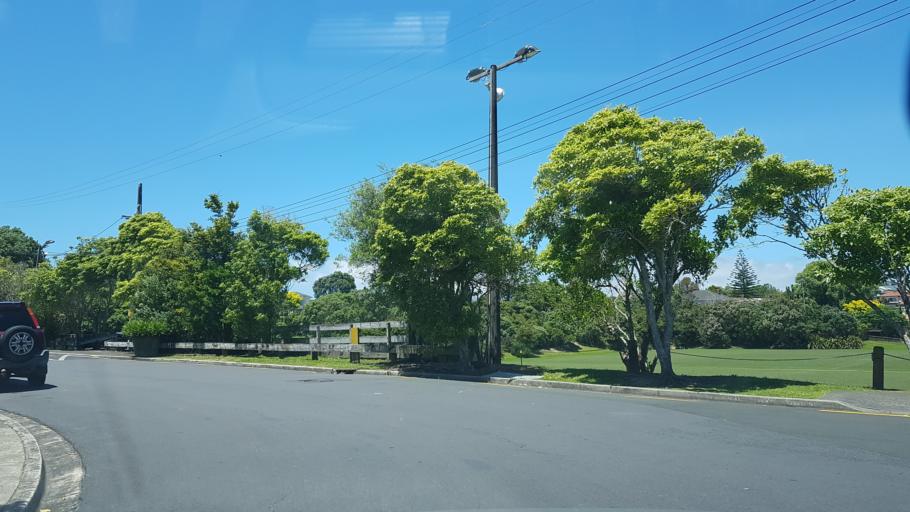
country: NZ
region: Auckland
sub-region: Auckland
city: North Shore
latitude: -36.8055
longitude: 174.7239
